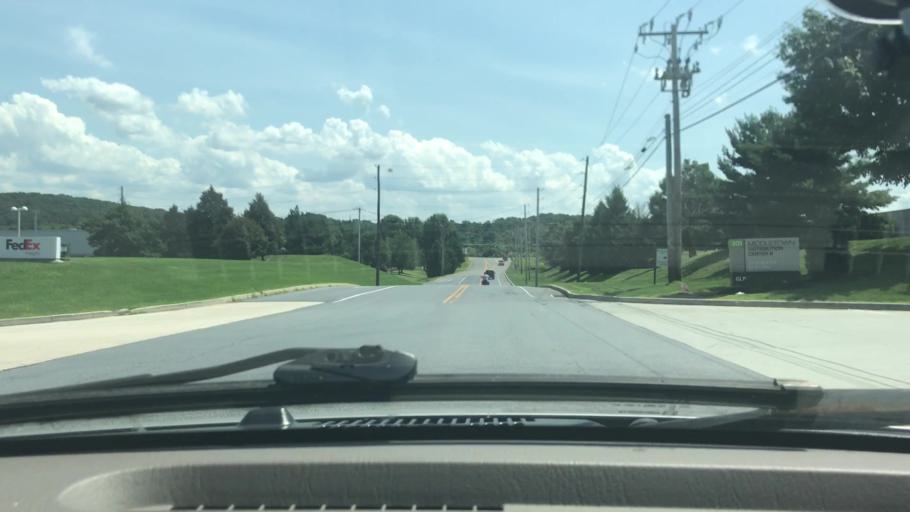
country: US
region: Pennsylvania
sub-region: Dauphin County
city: Middletown
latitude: 40.2335
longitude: -76.7378
